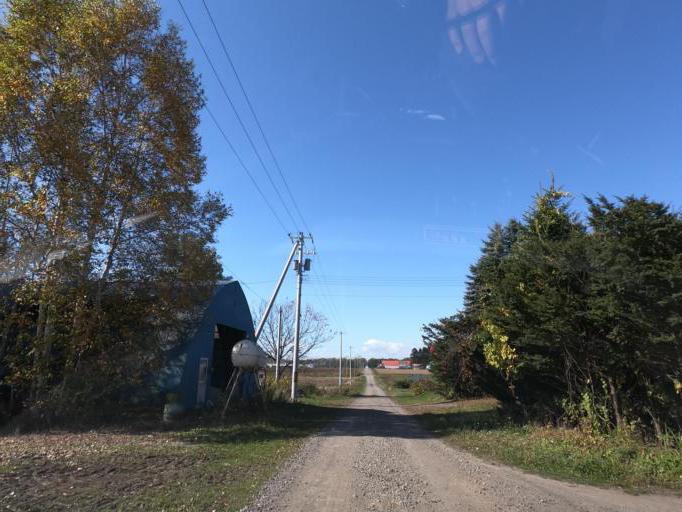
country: JP
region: Hokkaido
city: Otofuke
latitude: 43.0648
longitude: 143.2736
